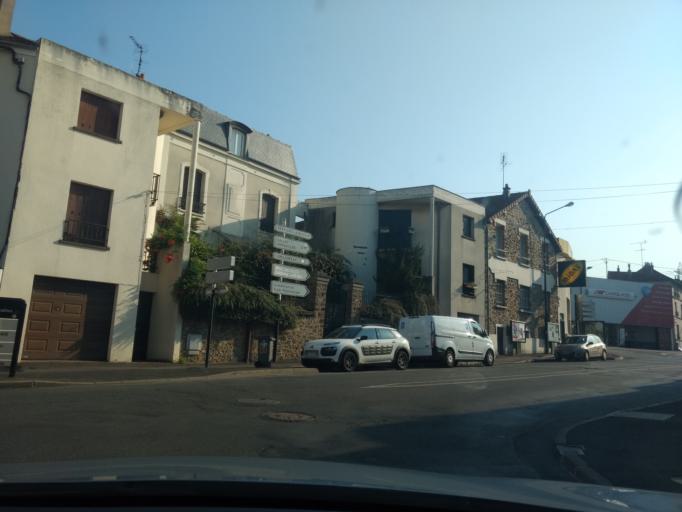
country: FR
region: Ile-de-France
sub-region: Departement de l'Essonne
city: Palaiseau
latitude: 48.7178
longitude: 2.2491
